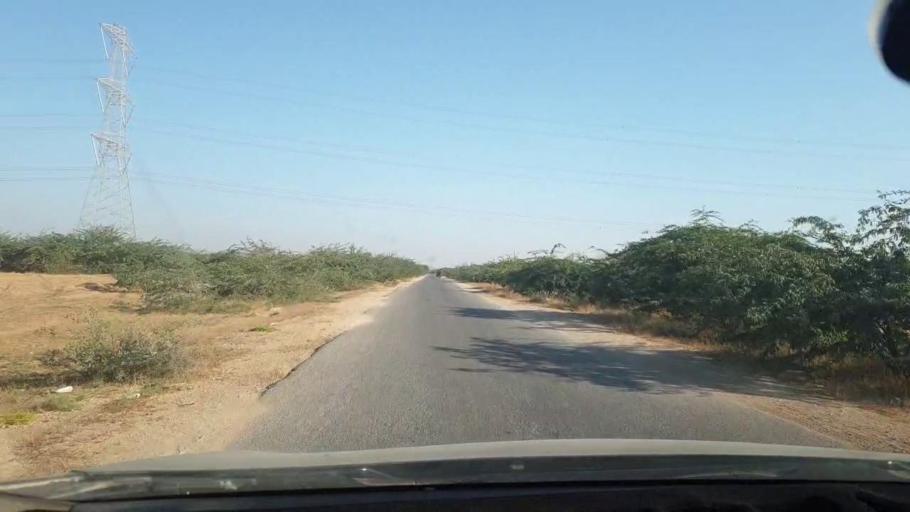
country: PK
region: Sindh
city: Malir Cantonment
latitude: 25.1606
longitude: 67.1942
